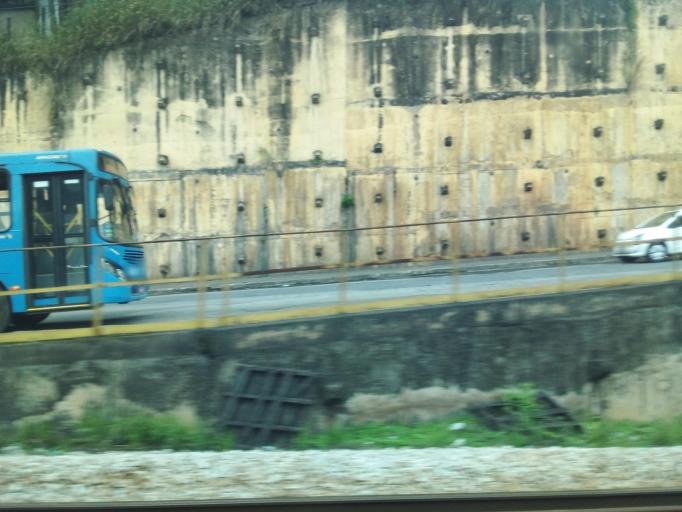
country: BR
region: Minas Gerais
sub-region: Joao Monlevade
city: Joao Monlevade
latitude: -19.8351
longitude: -43.1296
